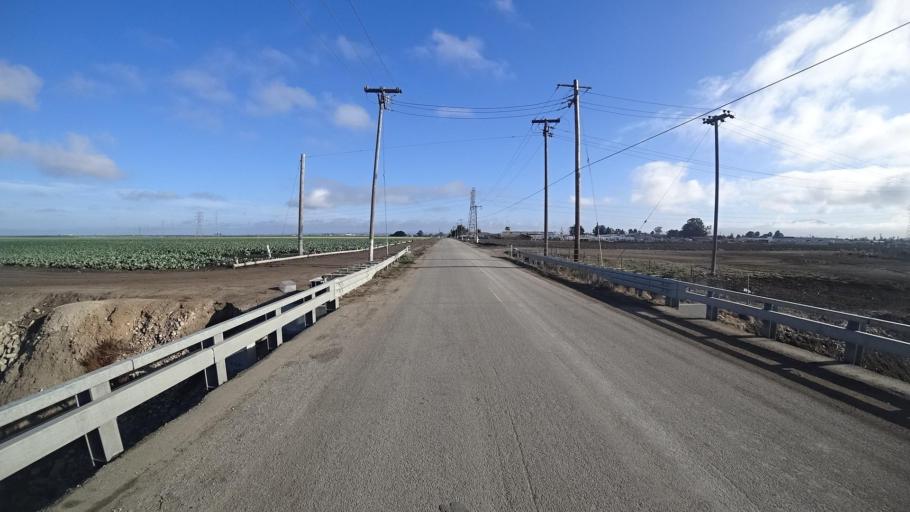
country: US
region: California
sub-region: Monterey County
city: Boronda
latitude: 36.6903
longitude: -121.6808
